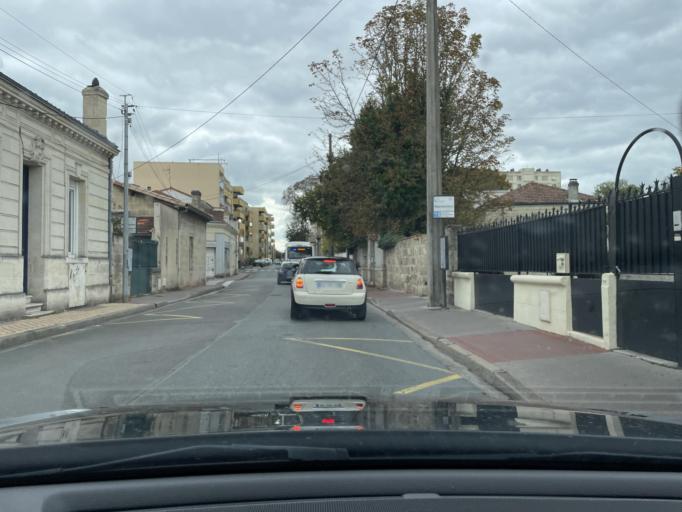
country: FR
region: Aquitaine
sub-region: Departement de la Gironde
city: Le Bouscat
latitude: 44.8619
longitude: -0.5900
